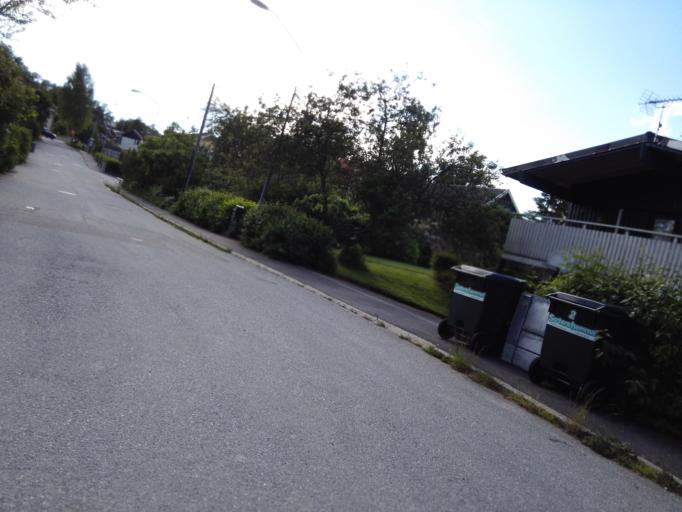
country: SE
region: Stockholm
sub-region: Huddinge Kommun
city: Segeltorp
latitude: 59.2725
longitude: 17.9550
